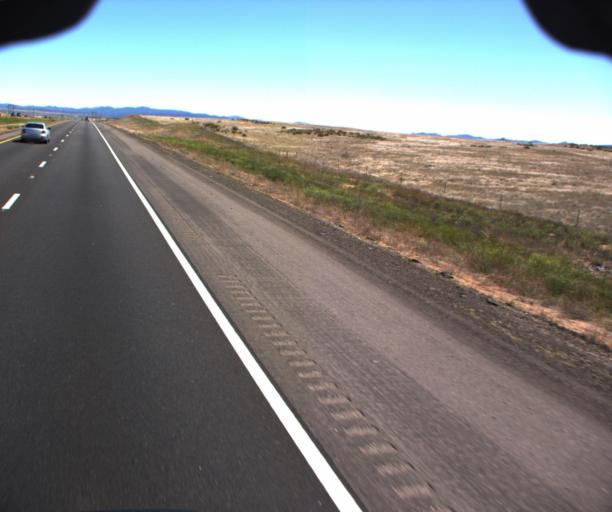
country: US
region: Arizona
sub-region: Yavapai County
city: Chino Valley
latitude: 34.6855
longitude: -112.4450
